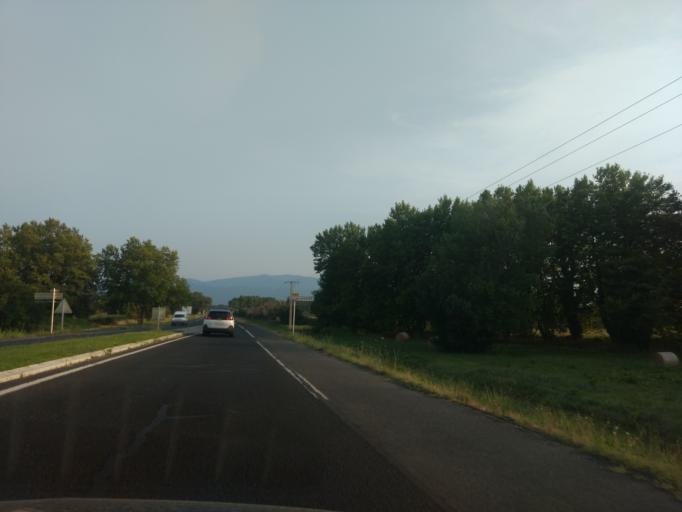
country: FR
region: Languedoc-Roussillon
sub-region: Departement des Pyrenees-Orientales
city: Saint-Cyprien-Plage
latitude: 42.6140
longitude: 3.0251
